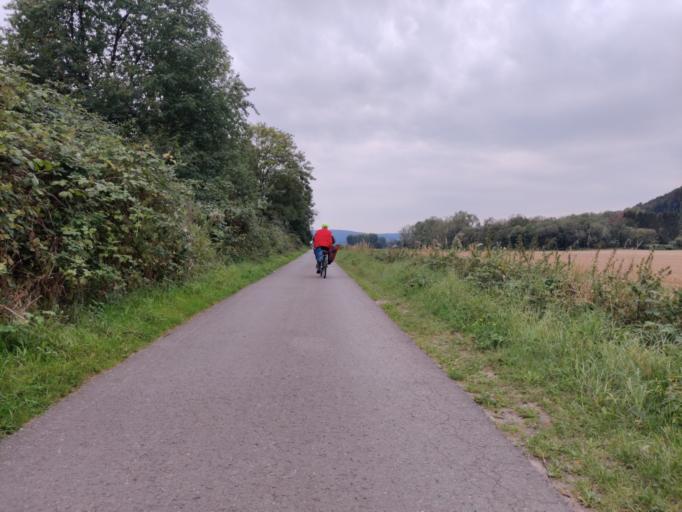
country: DE
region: Lower Saxony
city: Holzminden
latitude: 51.8446
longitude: 9.4485
